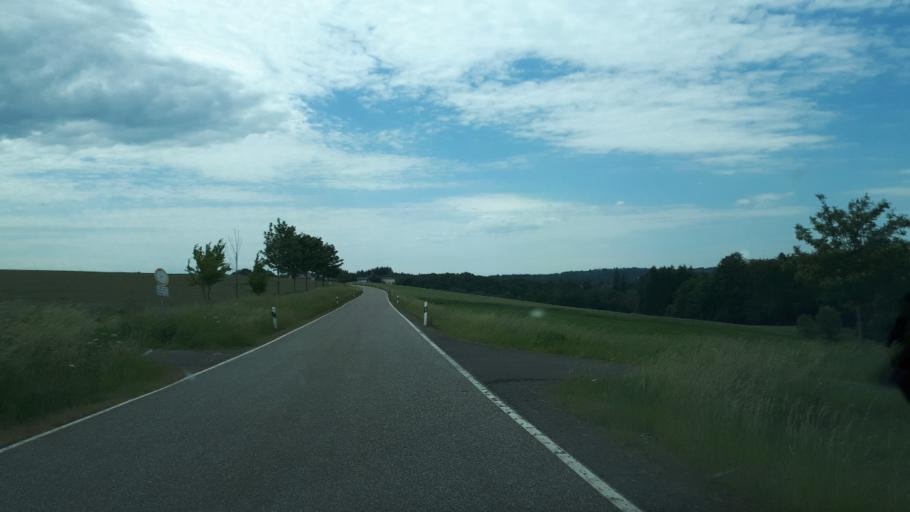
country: DE
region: Rheinland-Pfalz
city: Filz
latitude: 50.1758
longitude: 6.9870
